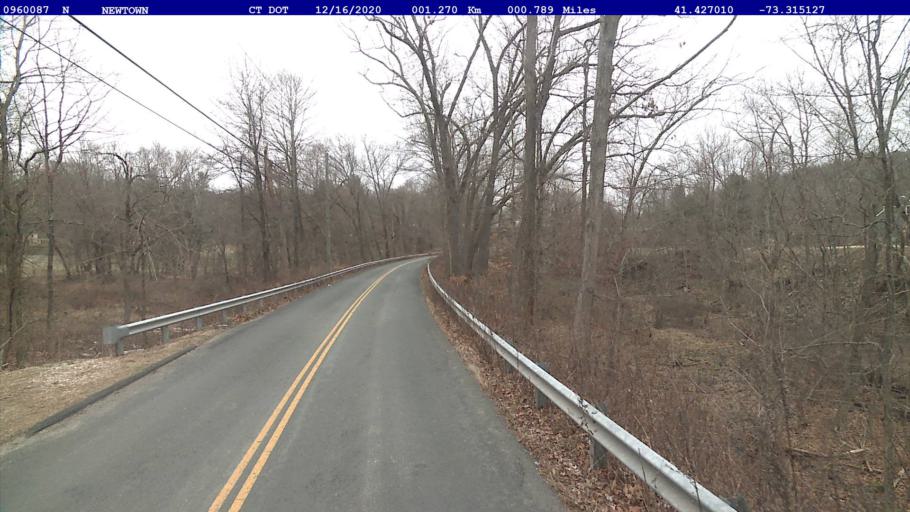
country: US
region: Connecticut
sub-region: Fairfield County
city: Newtown
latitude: 41.4270
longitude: -73.3151
